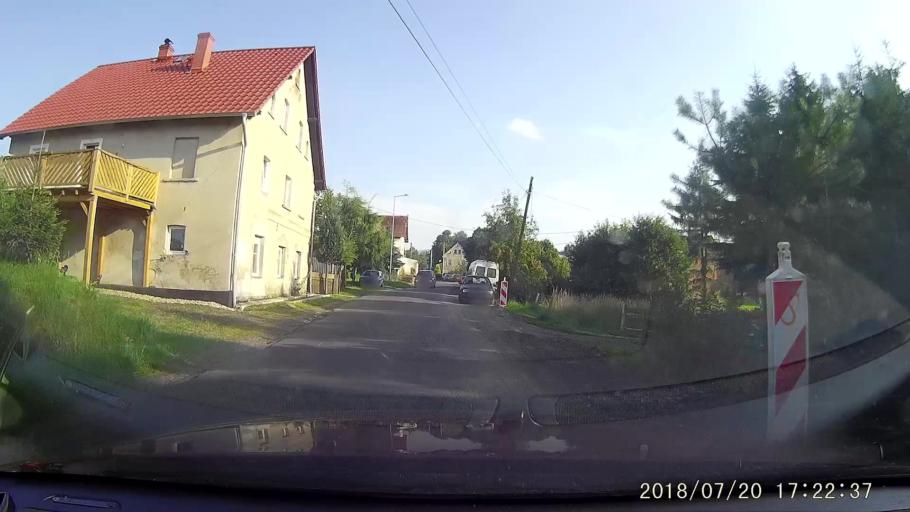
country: PL
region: Lower Silesian Voivodeship
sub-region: Powiat lubanski
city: Lesna
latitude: 50.9770
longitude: 15.2888
